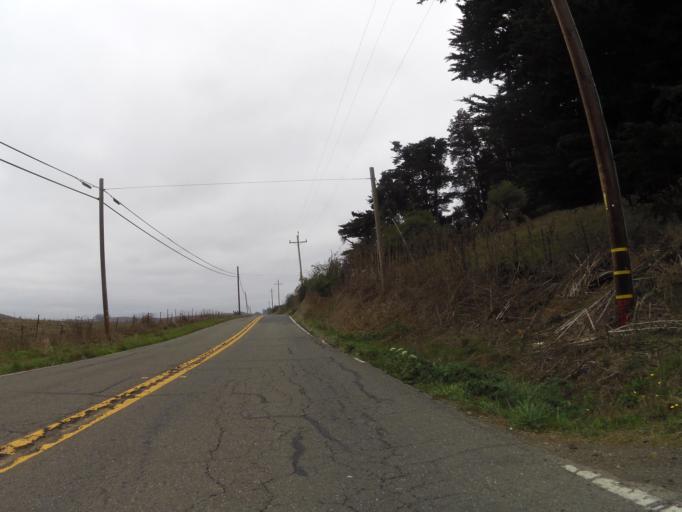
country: US
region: California
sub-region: Sonoma County
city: Occidental
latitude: 38.2910
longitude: -122.8991
